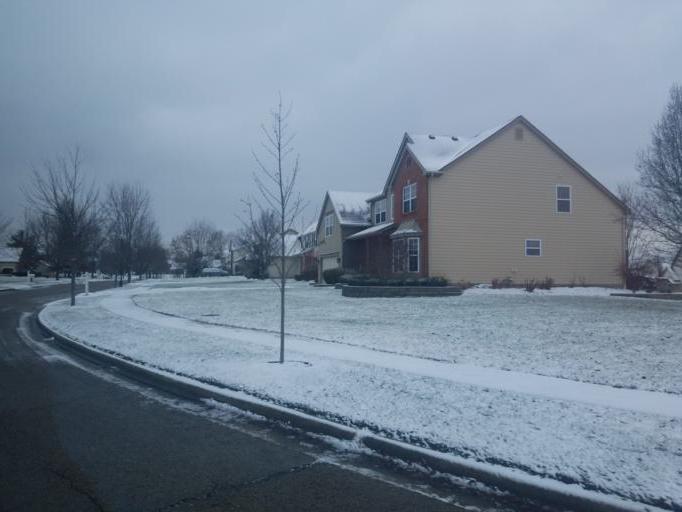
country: US
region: Ohio
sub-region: Franklin County
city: New Albany
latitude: 40.0473
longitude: -82.8218
